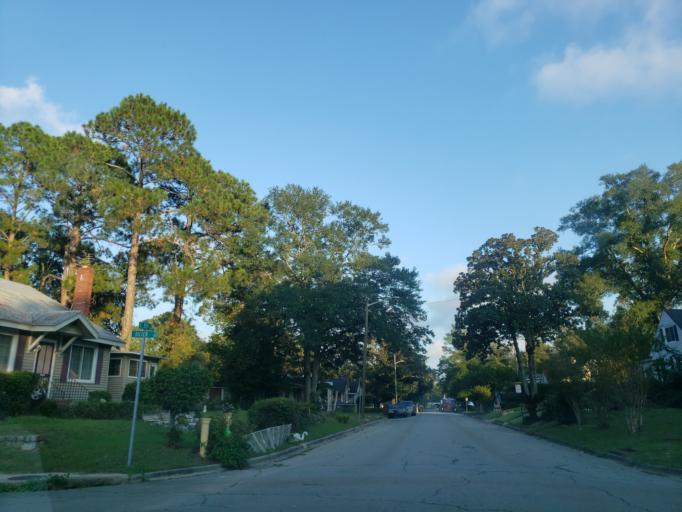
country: US
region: Georgia
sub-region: Chatham County
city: Thunderbolt
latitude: 32.0527
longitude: -81.0762
